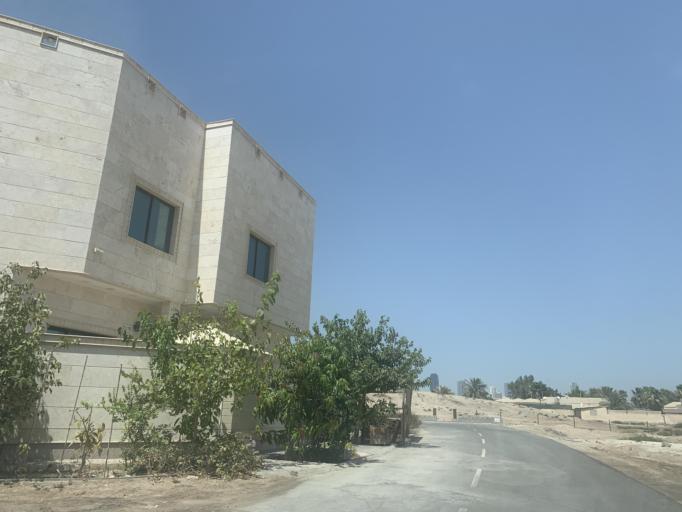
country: BH
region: Manama
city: Jidd Hafs
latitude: 26.2283
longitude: 50.5178
